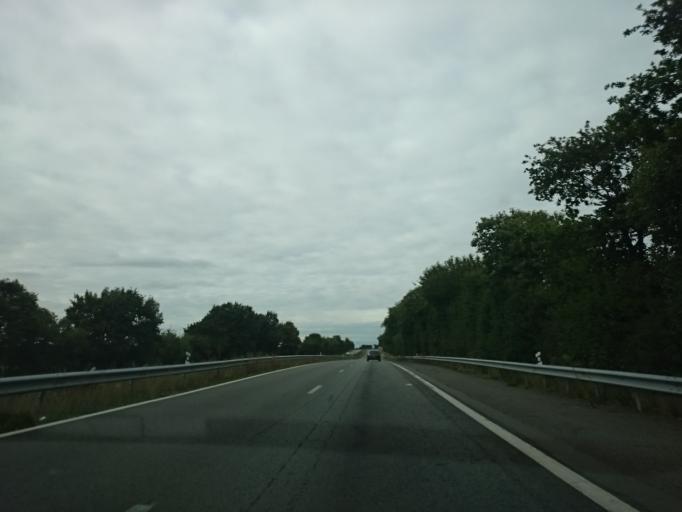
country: FR
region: Brittany
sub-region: Departement d'Ille-et-Vilaine
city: Grand-Fougeray
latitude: 47.7294
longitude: -1.7123
